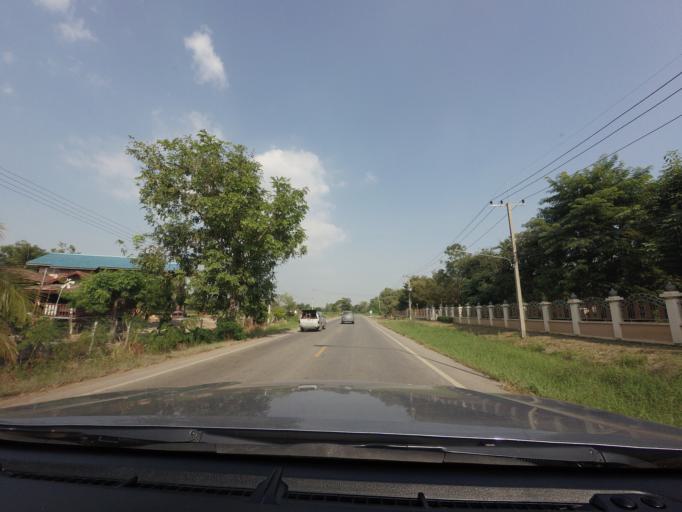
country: TH
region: Sukhothai
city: Kong Krailat
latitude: 16.9284
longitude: 99.9610
